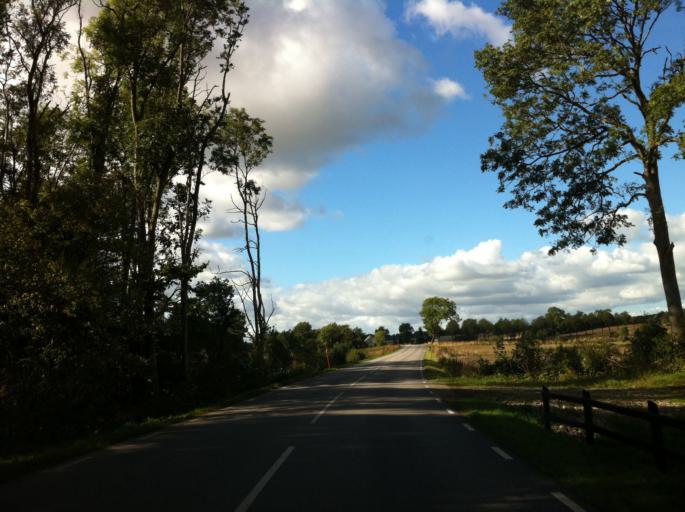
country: SE
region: Skane
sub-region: Tomelilla Kommun
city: Tomelilla
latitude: 55.6465
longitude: 13.9720
